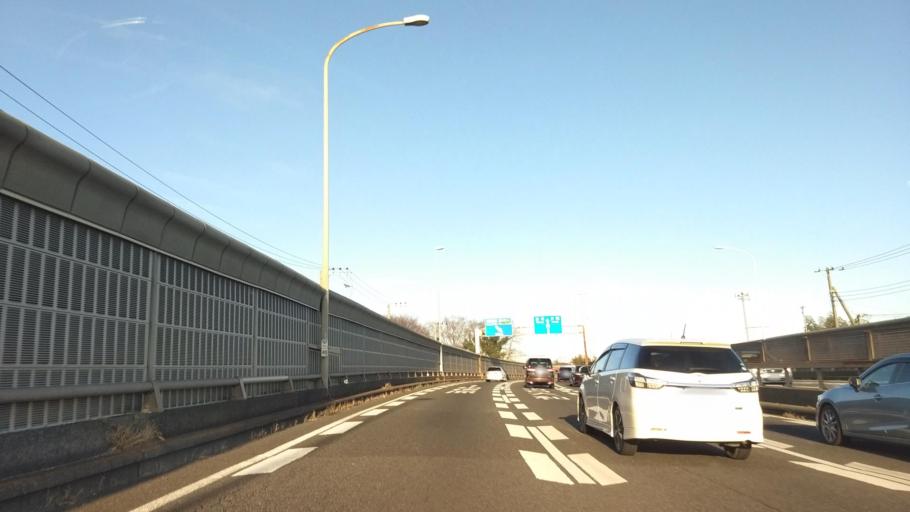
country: JP
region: Kanagawa
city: Atsugi
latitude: 35.4641
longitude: 139.3613
